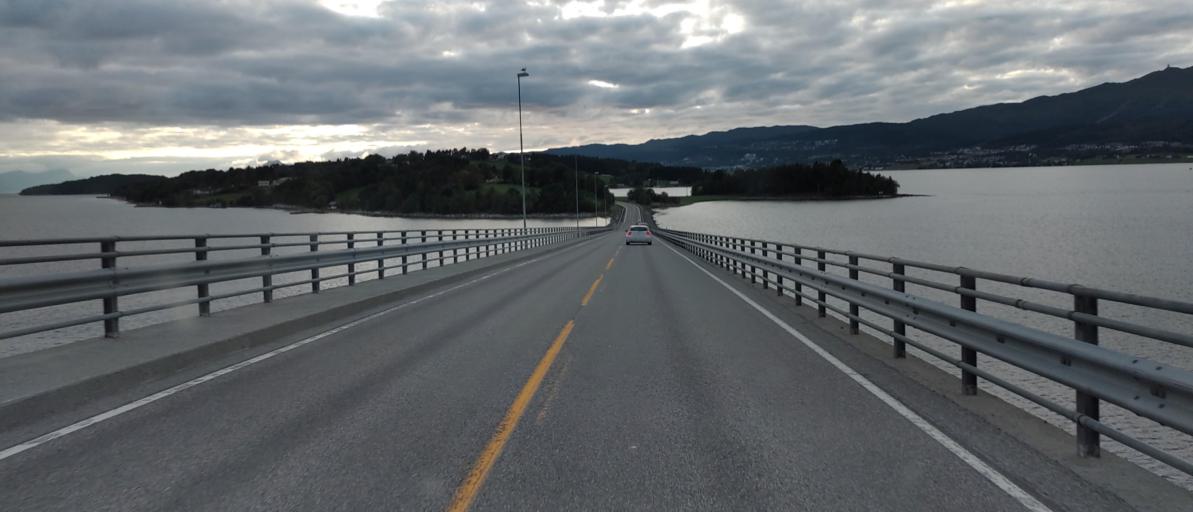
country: NO
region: More og Romsdal
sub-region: Molde
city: Hjelset
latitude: 62.7309
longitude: 7.3539
